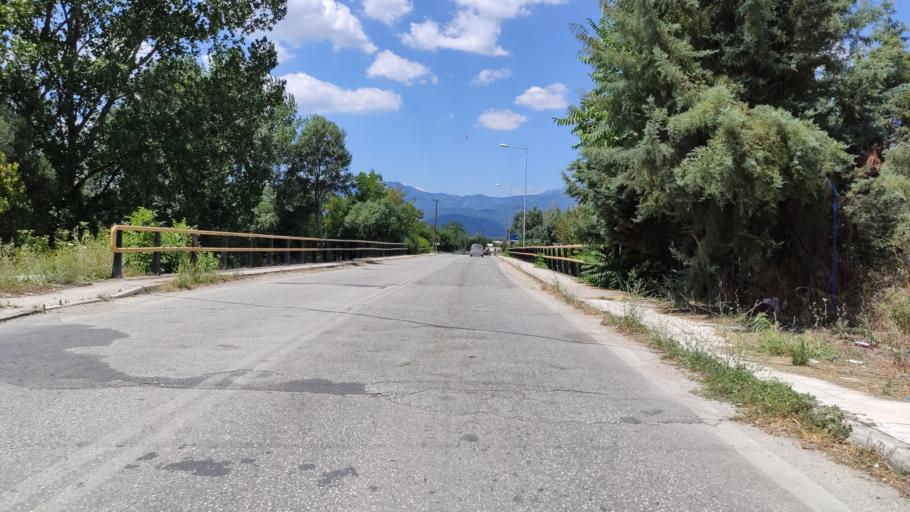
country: GR
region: East Macedonia and Thrace
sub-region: Nomos Rodopis
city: Komotini
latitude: 41.1270
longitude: 25.3854
